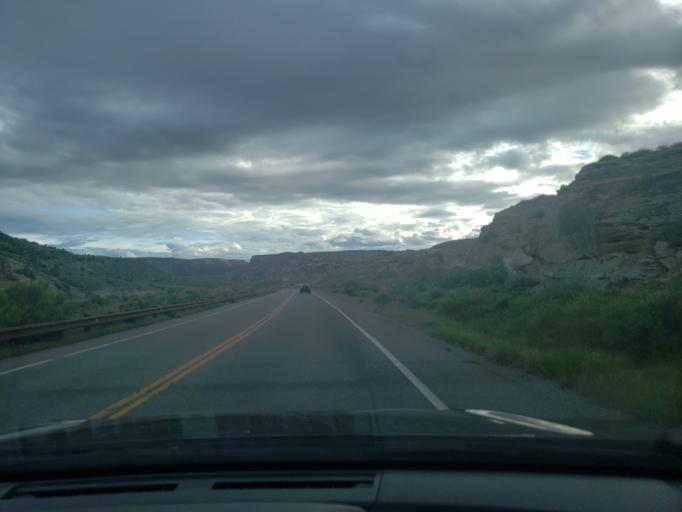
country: US
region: Colorado
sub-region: Mesa County
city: Redlands
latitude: 39.0565
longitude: -108.5972
